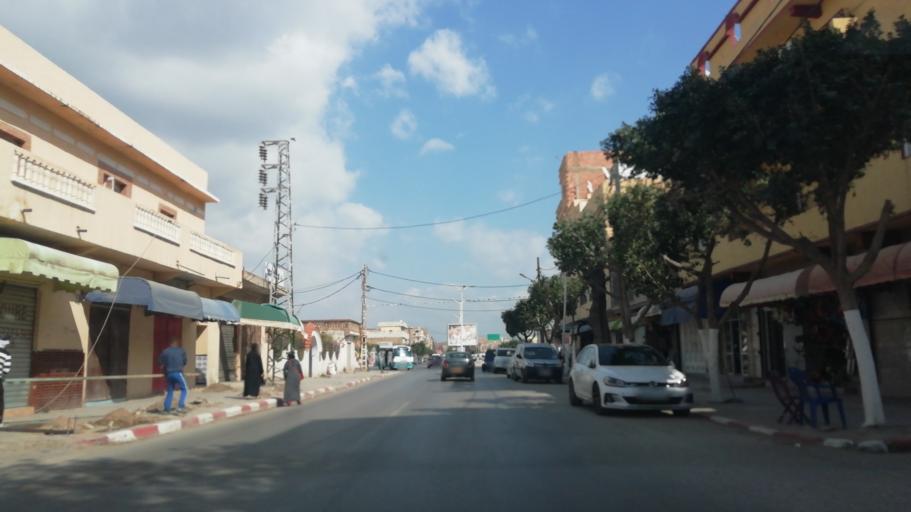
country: DZ
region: Mascara
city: Mascara
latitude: 35.5936
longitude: 0.0708
